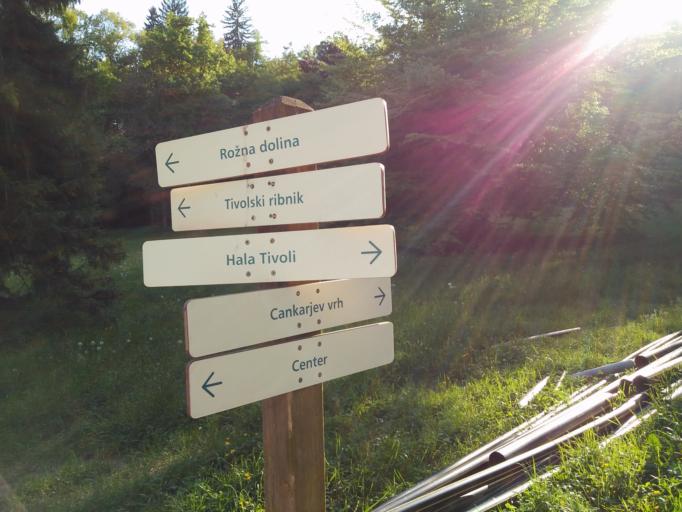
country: SI
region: Ljubljana
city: Ljubljana
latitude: 46.0545
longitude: 14.4926
